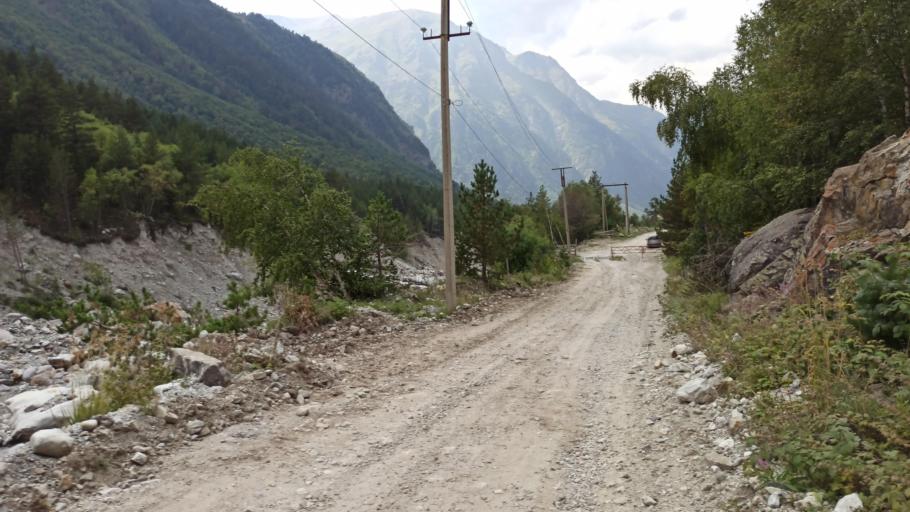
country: RU
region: Kabardino-Balkariya
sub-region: El'brusskiy Rayon
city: El'brus
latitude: 43.2208
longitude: 42.6864
